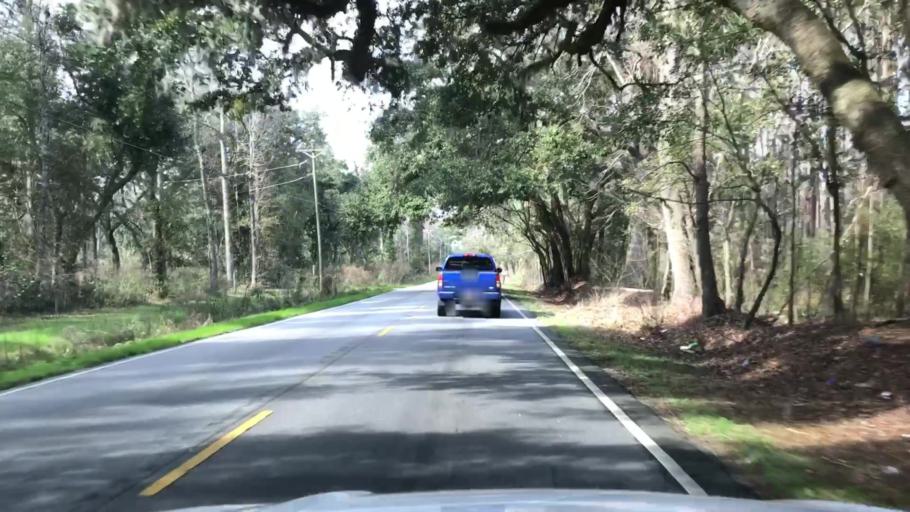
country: US
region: South Carolina
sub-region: Charleston County
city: Shell Point
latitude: 32.7743
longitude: -80.0860
